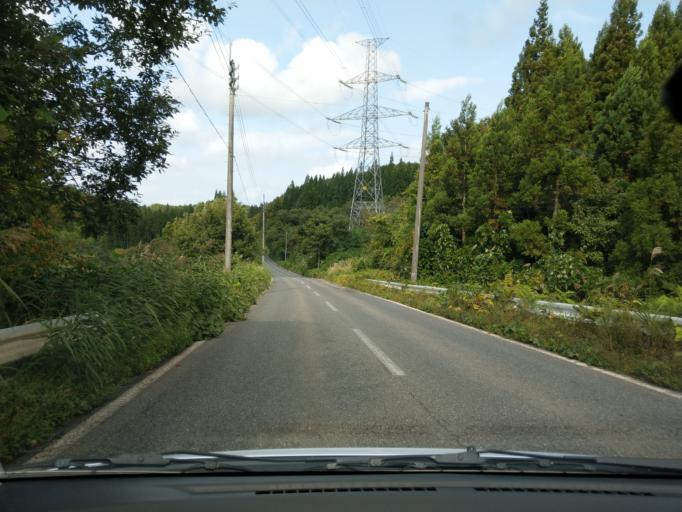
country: JP
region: Akita
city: Omagari
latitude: 39.4583
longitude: 140.3201
